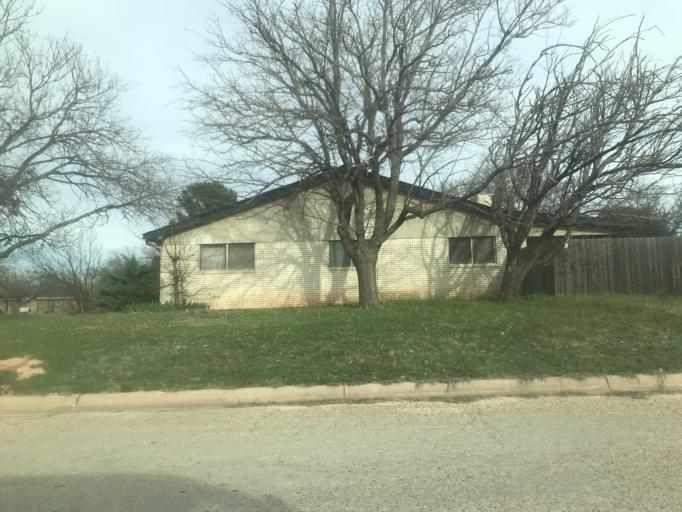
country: US
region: Texas
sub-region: Taylor County
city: Abilene
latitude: 32.3960
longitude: -99.7571
